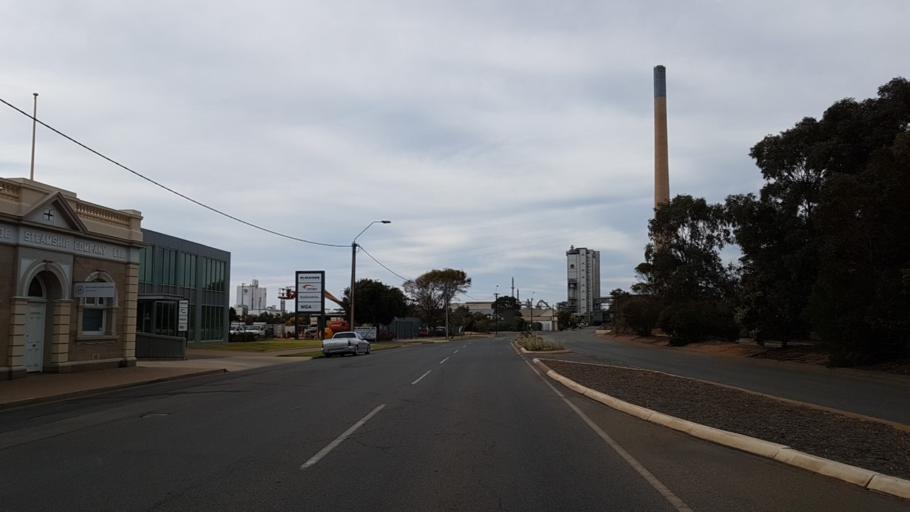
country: AU
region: South Australia
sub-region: Port Pirie City and Dists
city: Port Pirie
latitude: -33.1750
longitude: 138.0100
